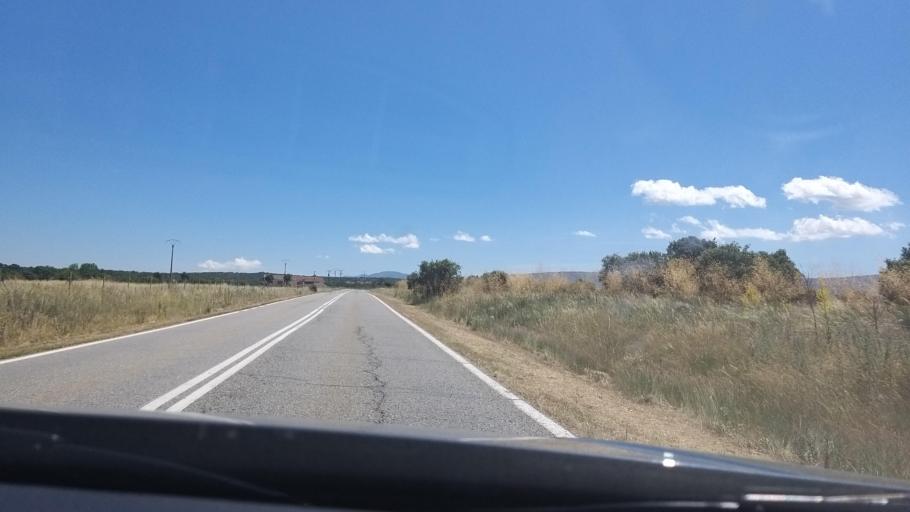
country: ES
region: Castille and Leon
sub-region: Provincia de Segovia
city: Pedraza
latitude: 41.1297
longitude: -3.7920
